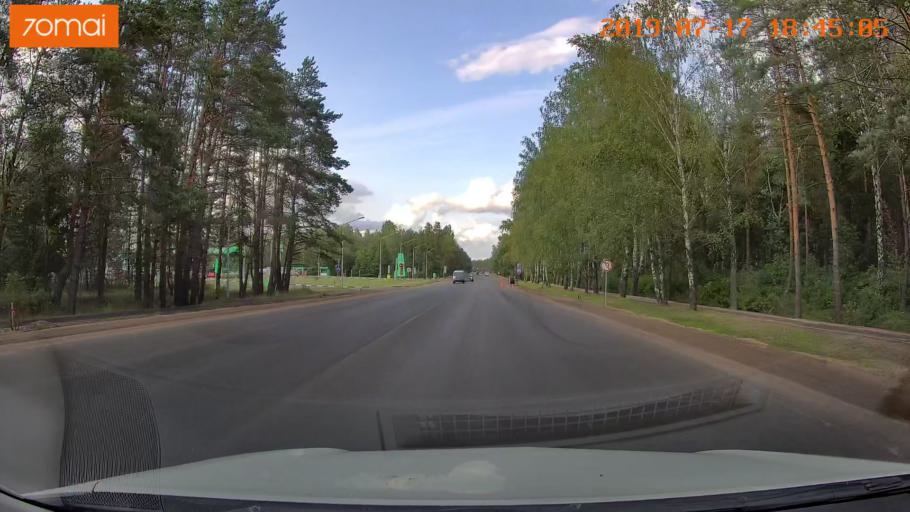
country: BY
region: Mogilev
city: Asipovichy
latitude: 53.3223
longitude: 28.6511
